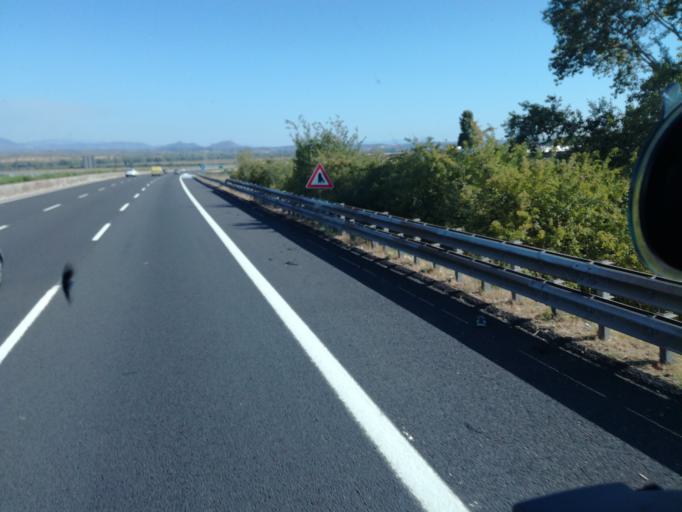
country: IT
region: Latium
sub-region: Citta metropolitana di Roma Capitale
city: Fiano Romano
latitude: 42.1609
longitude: 12.6203
